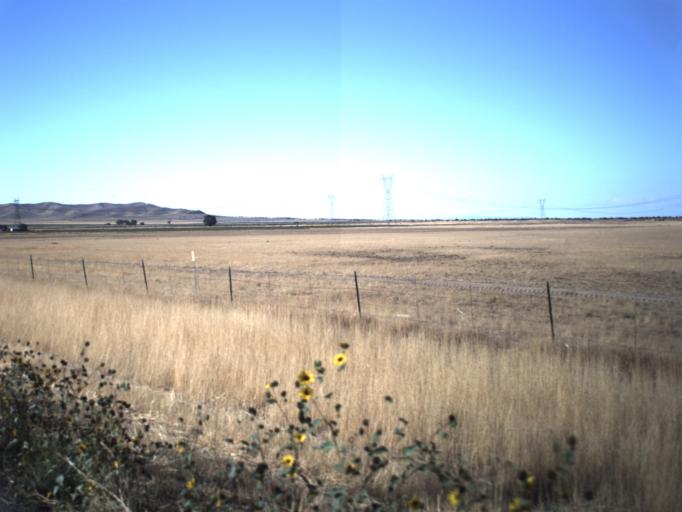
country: US
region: Utah
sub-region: Millard County
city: Delta
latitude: 39.5001
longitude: -112.2690
